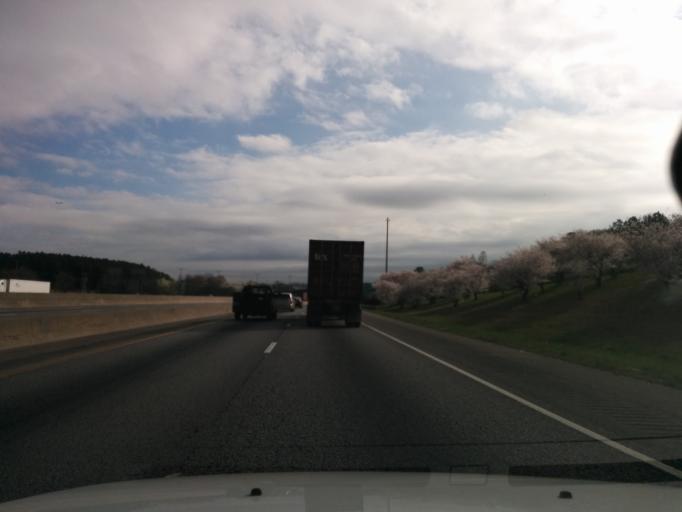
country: US
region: Georgia
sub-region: Fulton County
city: Hapeville
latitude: 33.6298
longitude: -84.4140
